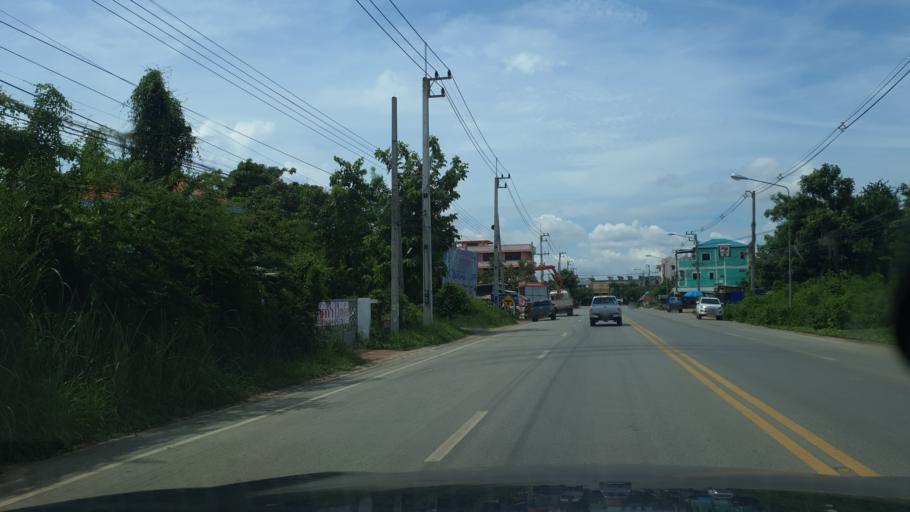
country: TH
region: Sukhothai
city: Sukhothai
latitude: 17.0246
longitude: 99.8161
